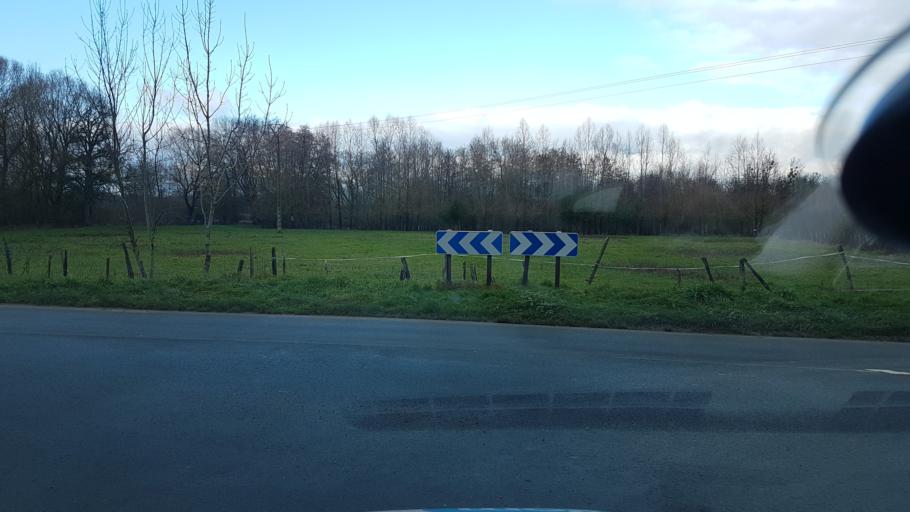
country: FR
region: Ile-de-France
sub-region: Departement de Seine-et-Marne
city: Montigny-sur-Loing
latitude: 48.2760
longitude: 2.7971
